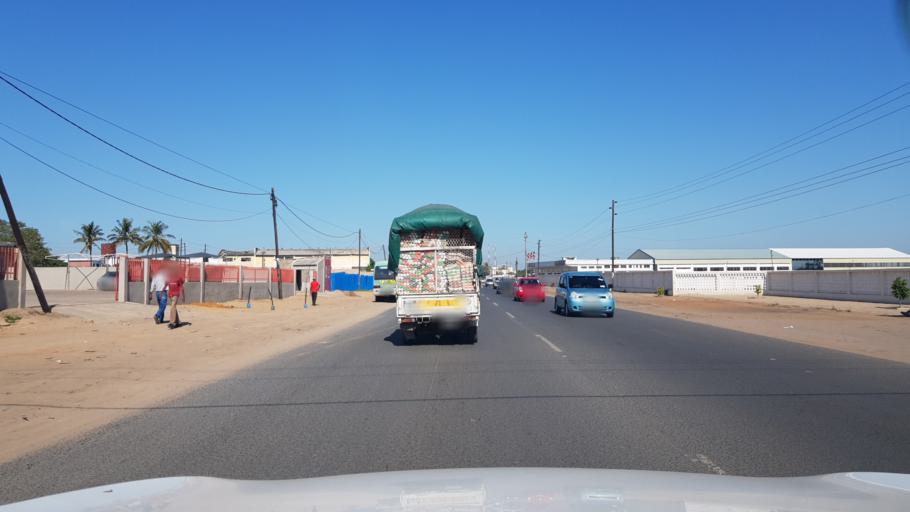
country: MZ
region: Maputo City
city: Maputo
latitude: -25.8621
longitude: 32.5666
